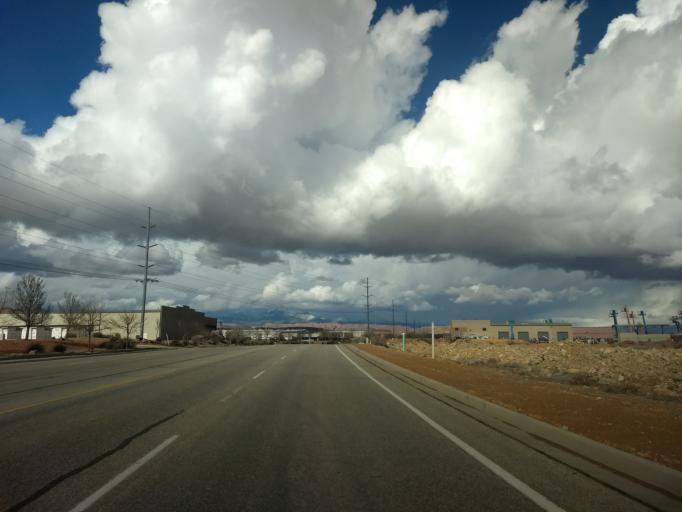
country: US
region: Utah
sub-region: Washington County
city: Saint George
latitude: 37.0324
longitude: -113.5617
